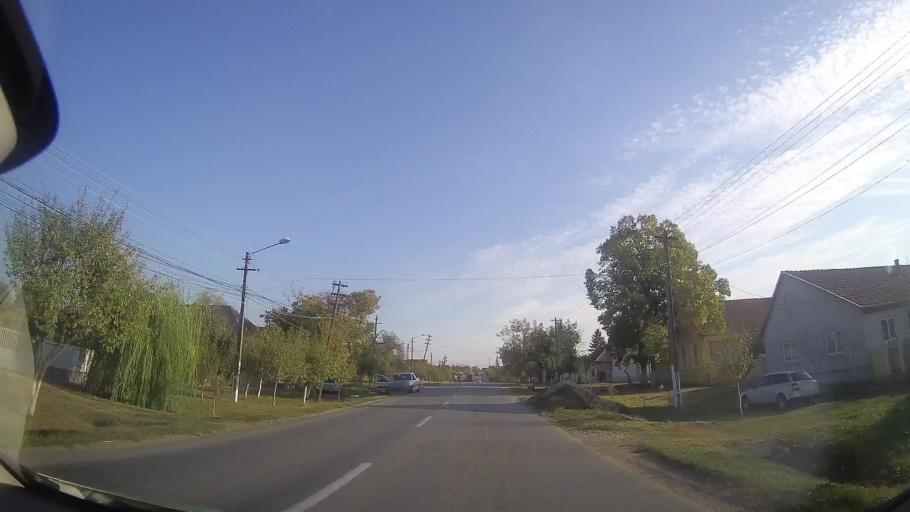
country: RO
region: Timis
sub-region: Comuna Fibis
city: Fibis
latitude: 45.9747
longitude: 21.4231
